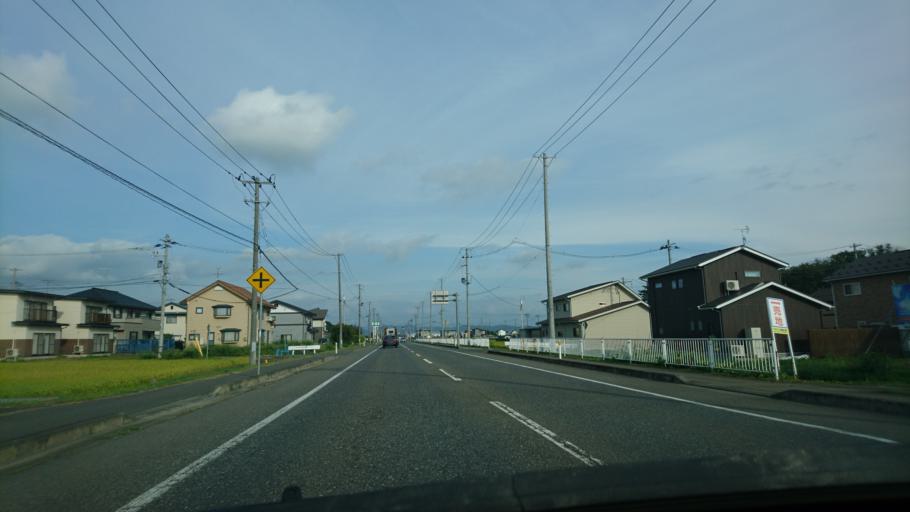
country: JP
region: Iwate
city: Kitakami
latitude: 39.3046
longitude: 141.0352
